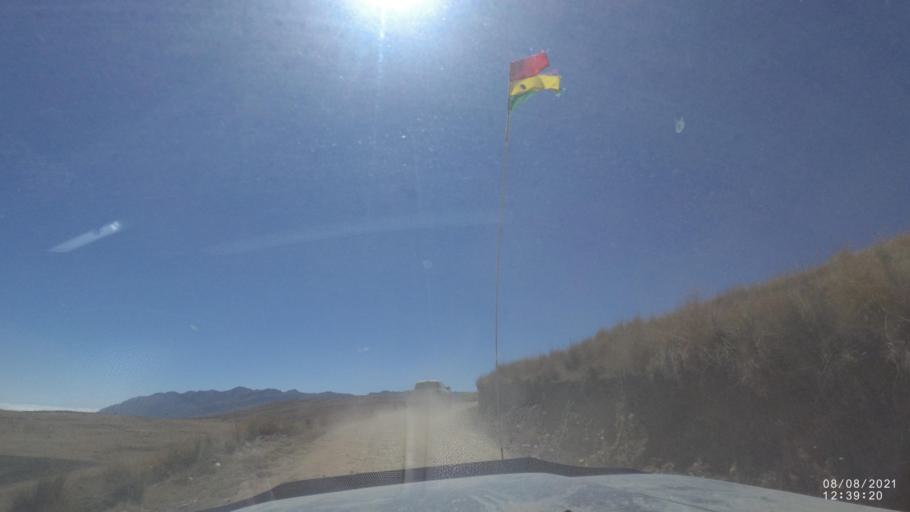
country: BO
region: Cochabamba
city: Colchani
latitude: -16.8286
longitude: -66.6246
